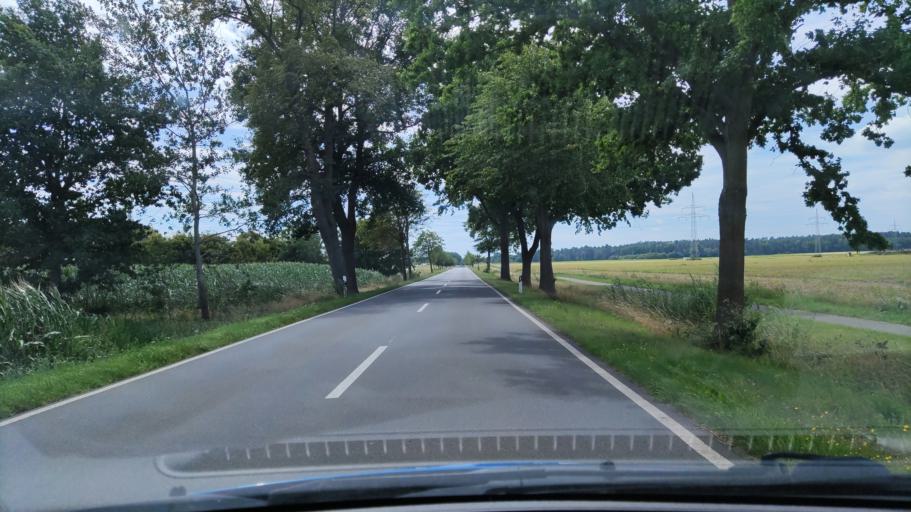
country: DE
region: Lower Saxony
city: Clenze
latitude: 52.9264
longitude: 10.9495
